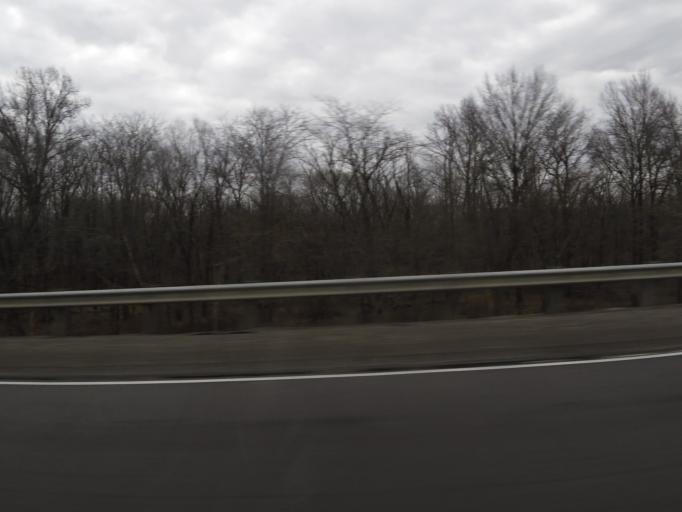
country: US
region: Illinois
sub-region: Franklin County
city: West Frankfort
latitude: 37.9296
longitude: -88.9465
